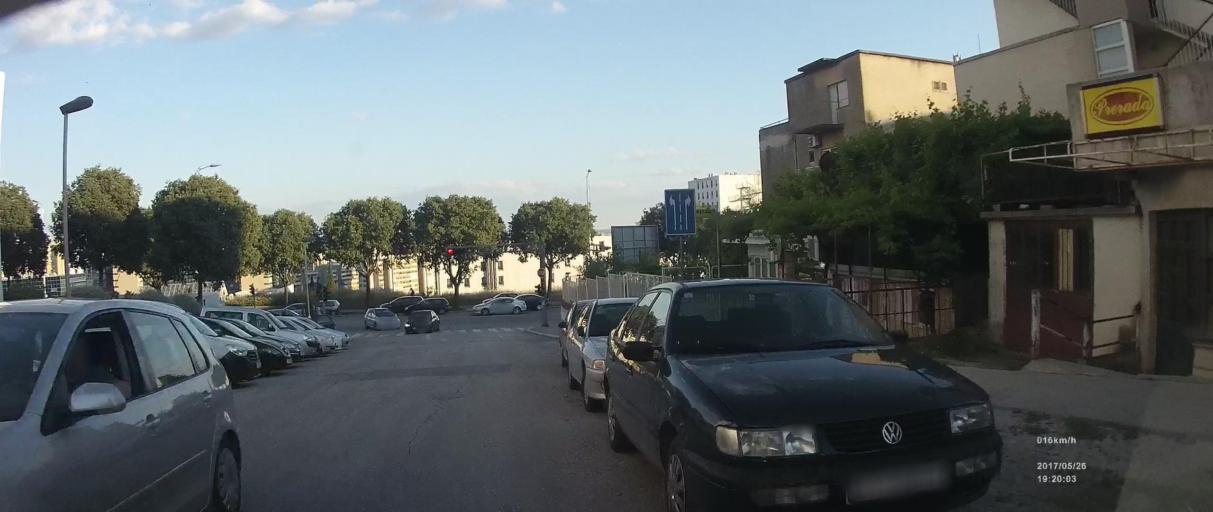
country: HR
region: Splitsko-Dalmatinska
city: Vranjic
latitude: 43.5138
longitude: 16.4659
